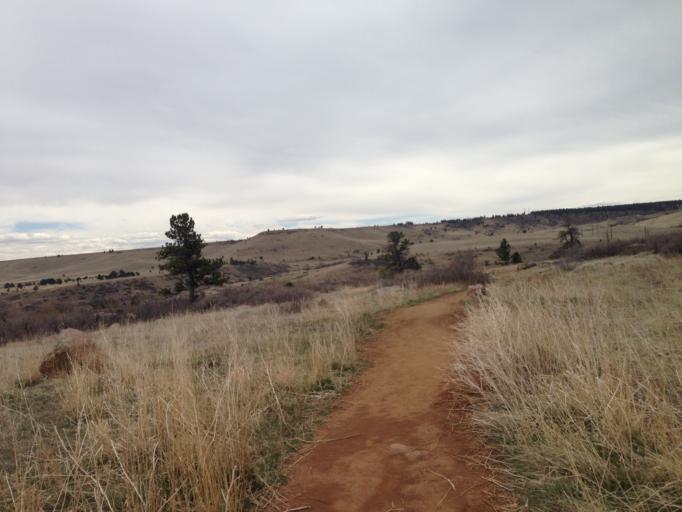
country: US
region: Colorado
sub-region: Boulder County
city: Boulder
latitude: 39.9438
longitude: -105.2629
